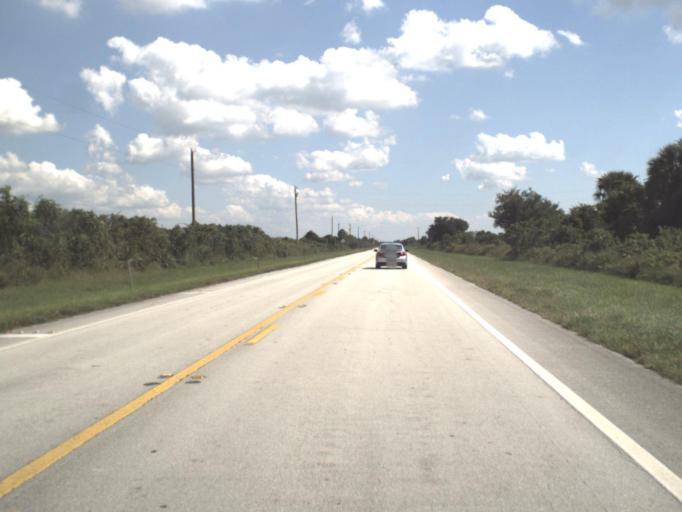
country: US
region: Florida
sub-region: Highlands County
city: Lake Placid
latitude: 27.3980
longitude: -81.1601
